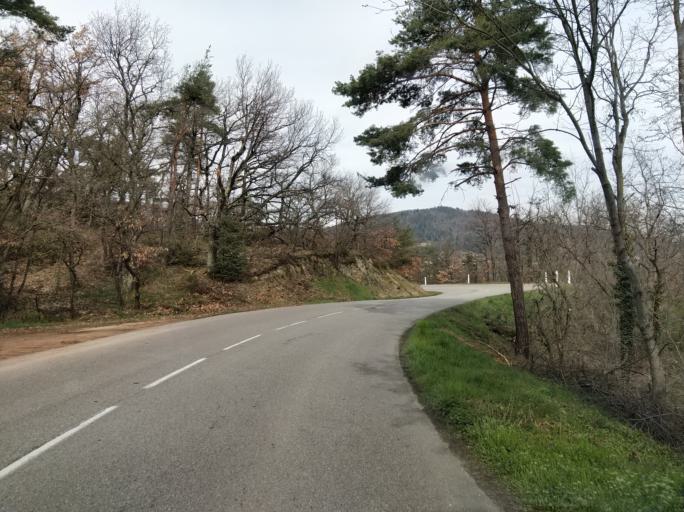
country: FR
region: Rhone-Alpes
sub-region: Departement de l'Ardeche
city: Satillieu
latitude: 45.1812
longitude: 4.6426
